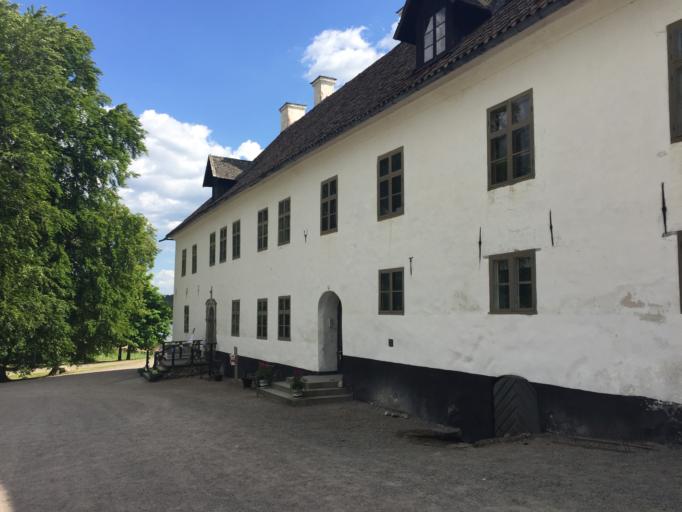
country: SE
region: Stockholm
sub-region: Sigtuna Kommun
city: Sigtuna
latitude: 59.7039
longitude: 17.6215
